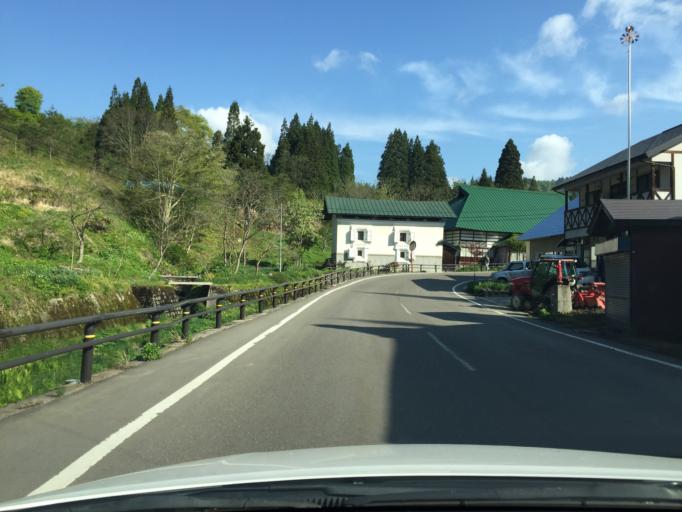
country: JP
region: Fukushima
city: Kitakata
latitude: 37.6918
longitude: 139.7147
